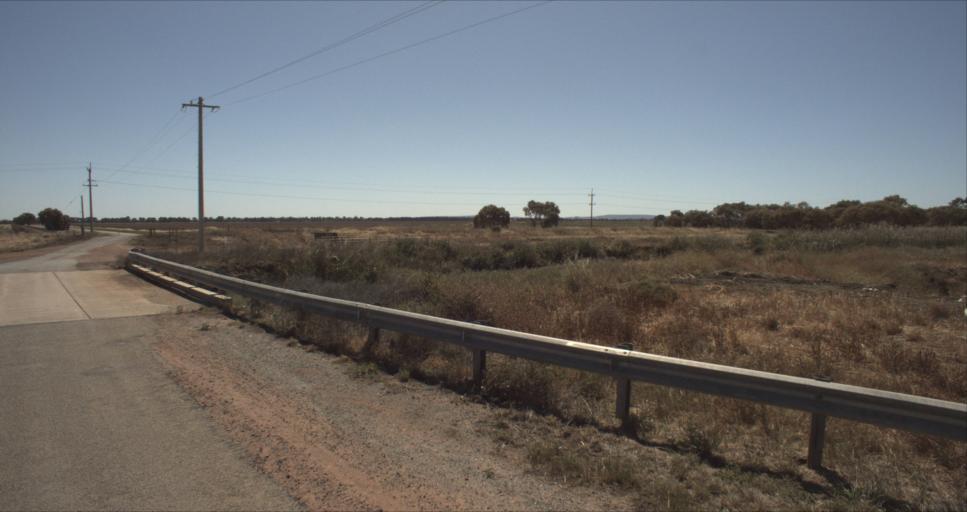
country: AU
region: New South Wales
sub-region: Leeton
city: Leeton
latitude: -34.5680
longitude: 146.3112
